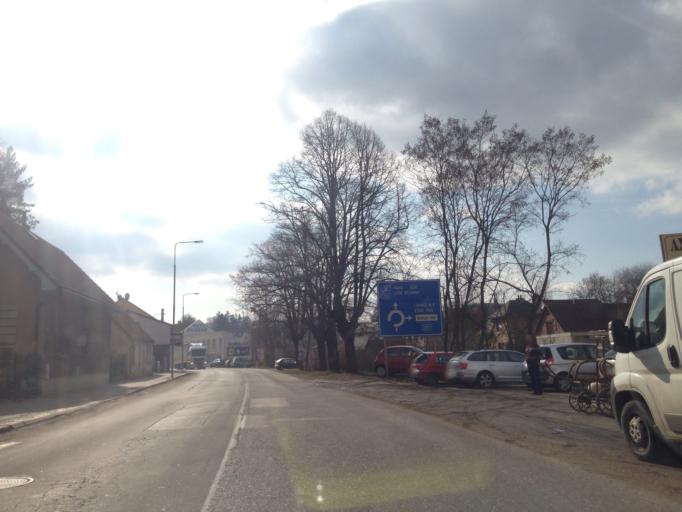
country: CZ
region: Kralovehradecky
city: Nova Paka
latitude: 50.4962
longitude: 15.5230
